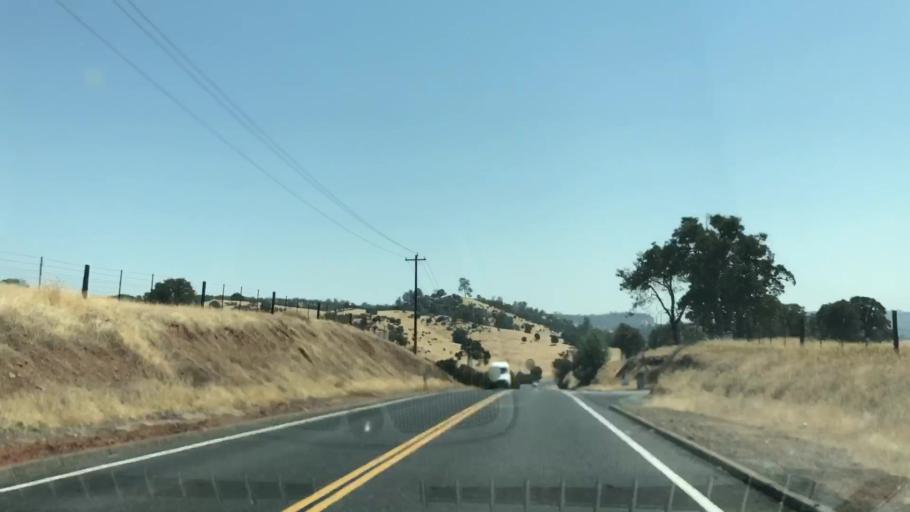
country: US
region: California
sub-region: Calaveras County
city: Copperopolis
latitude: 37.9304
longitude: -120.6001
